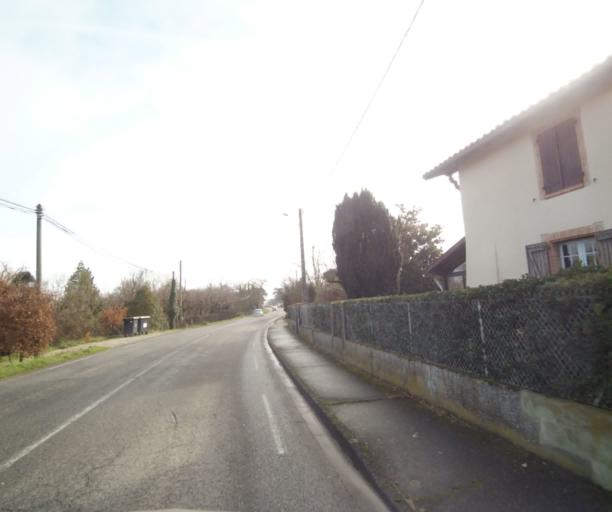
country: FR
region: Midi-Pyrenees
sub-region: Departement de la Haute-Garonne
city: Villemur-sur-Tarn
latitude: 43.8616
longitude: 1.4809
